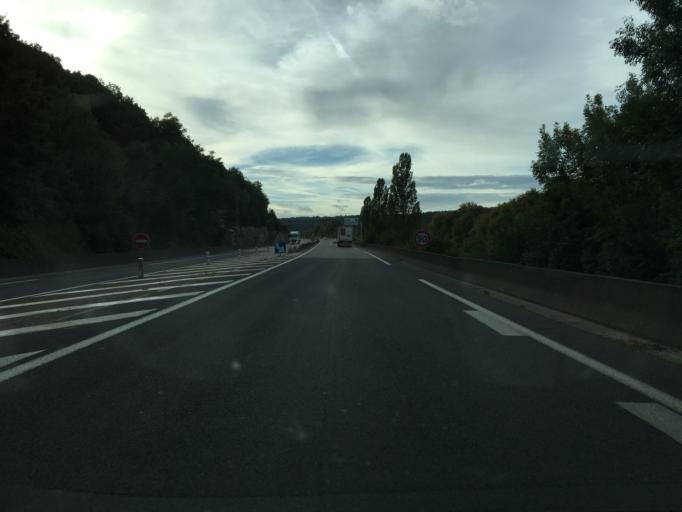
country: FR
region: Bourgogne
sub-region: Departement de la Cote-d'Or
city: Plombieres-les-Dijon
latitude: 47.3345
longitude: 4.9749
